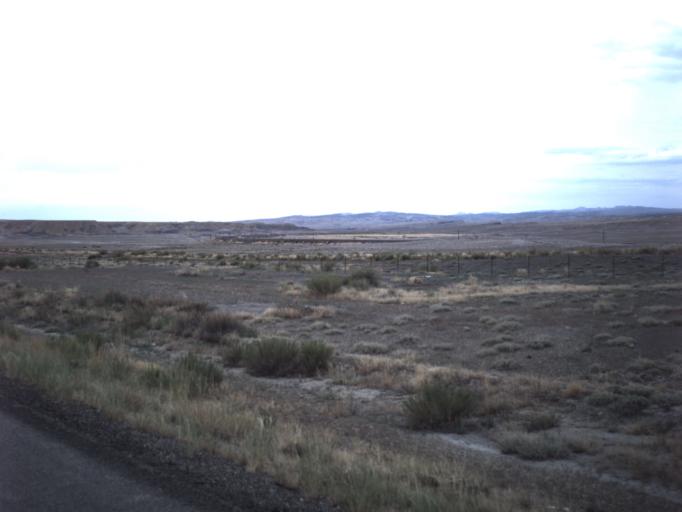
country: US
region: Utah
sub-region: Carbon County
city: East Carbon City
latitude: 39.3561
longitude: -110.3848
